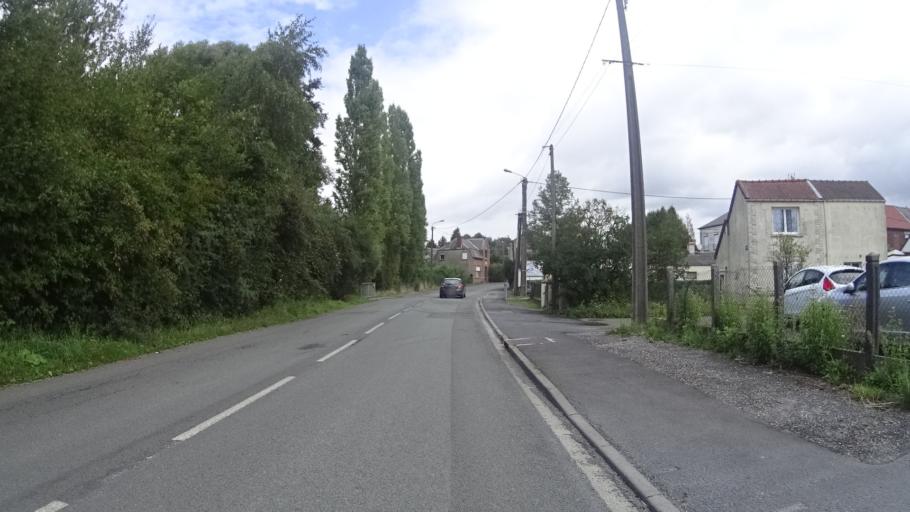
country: FR
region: Nord-Pas-de-Calais
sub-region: Departement du Nord
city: Berlaimont
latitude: 50.1961
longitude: 3.8092
